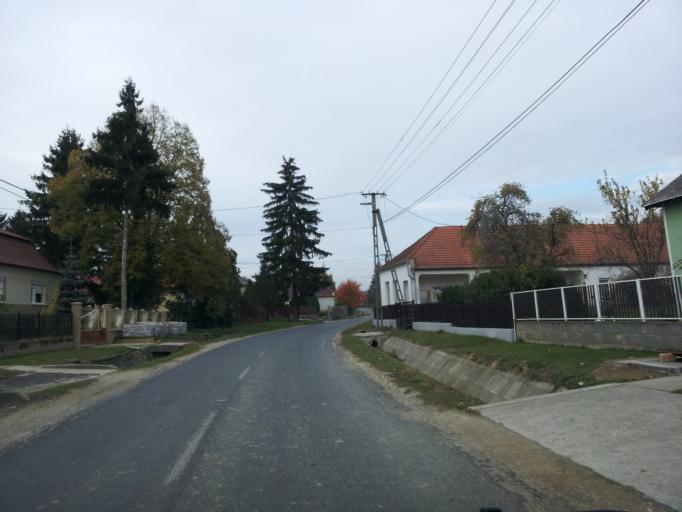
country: HU
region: Gyor-Moson-Sopron
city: Pannonhalma
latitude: 47.4782
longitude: 17.7034
